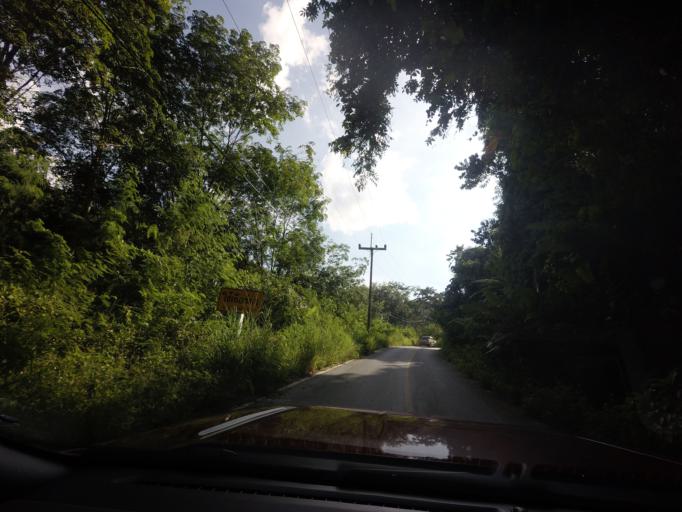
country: TH
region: Yala
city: Than To
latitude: 6.0649
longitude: 101.3603
